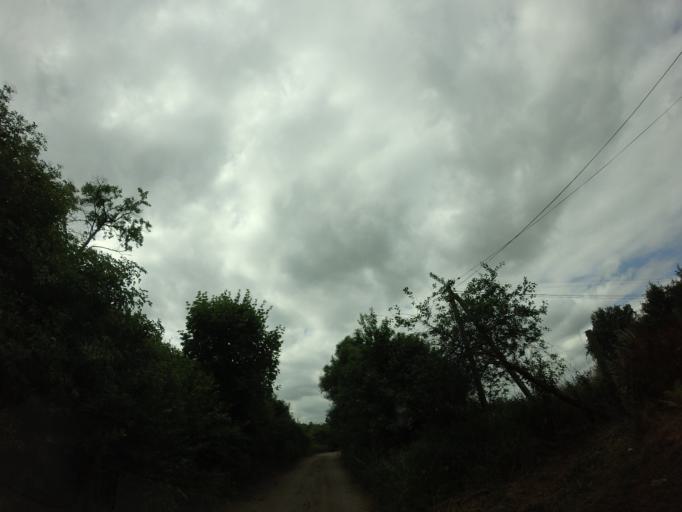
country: PL
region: Lubusz
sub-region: Powiat strzelecko-drezdenecki
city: Strzelce Krajenskie
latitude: 52.9463
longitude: 15.6088
